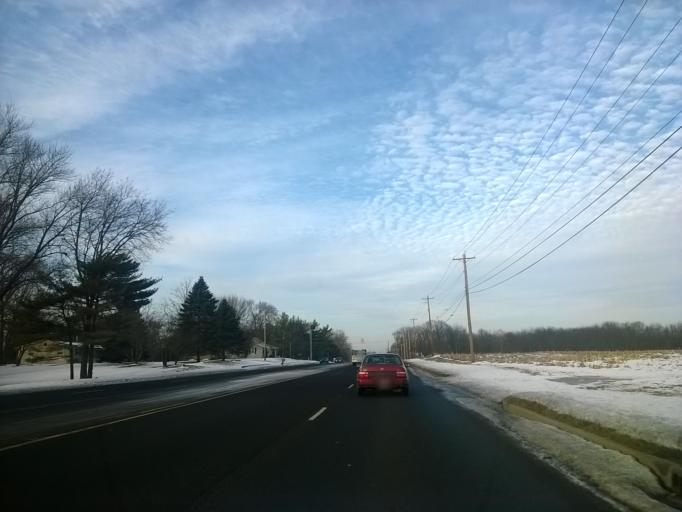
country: US
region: Indiana
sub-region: Hamilton County
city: Carmel
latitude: 40.0003
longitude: -86.0804
